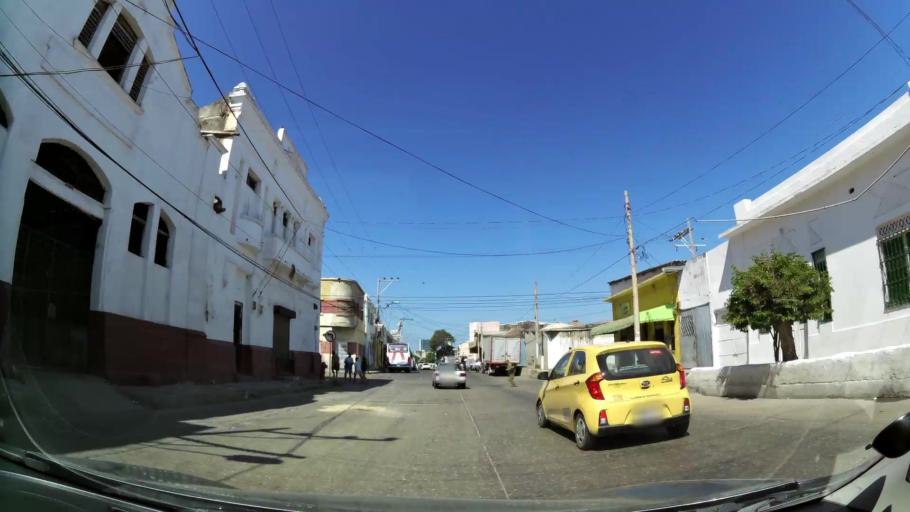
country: CO
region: Atlantico
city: Barranquilla
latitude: 10.9752
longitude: -74.7826
